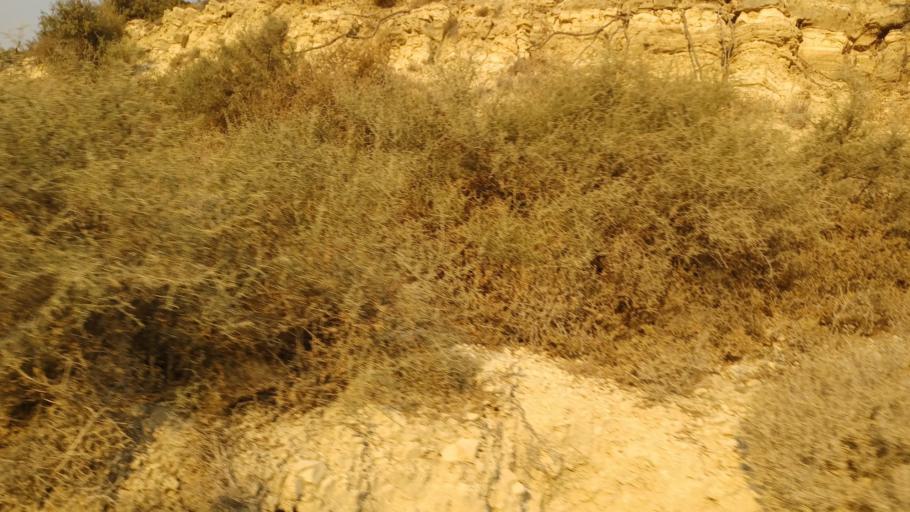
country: CY
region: Limassol
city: Pissouri
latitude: 34.6972
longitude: 32.6610
